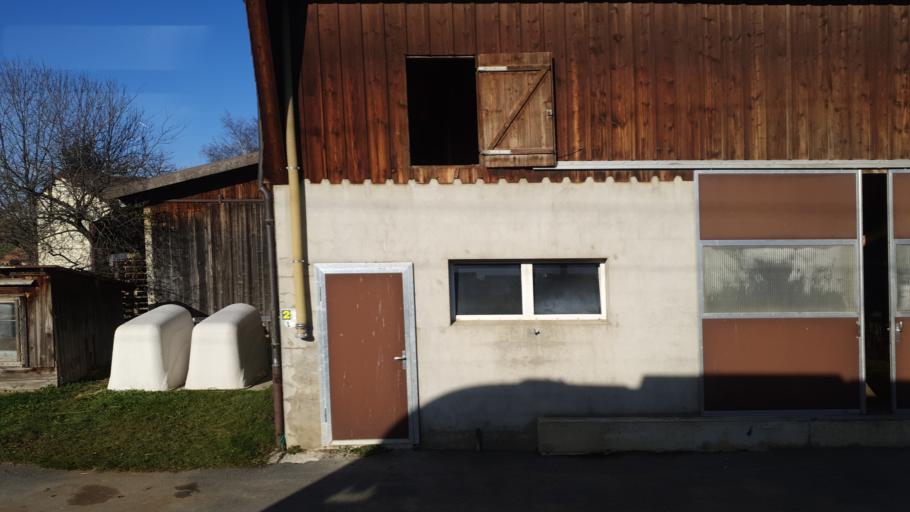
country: CH
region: Fribourg
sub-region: Gruyere District
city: Vuadens
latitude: 46.6165
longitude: 7.0074
